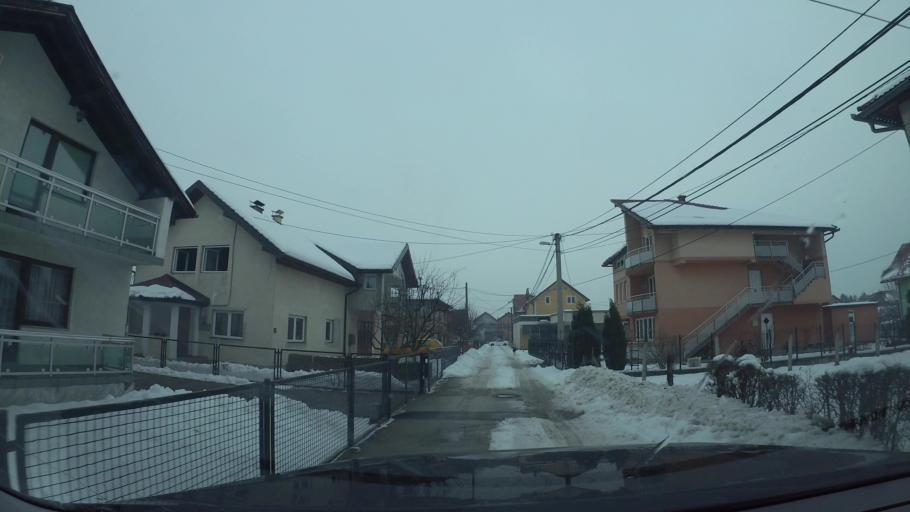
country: BA
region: Federation of Bosnia and Herzegovina
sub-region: Kanton Sarajevo
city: Sarajevo
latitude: 43.8482
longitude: 18.3058
